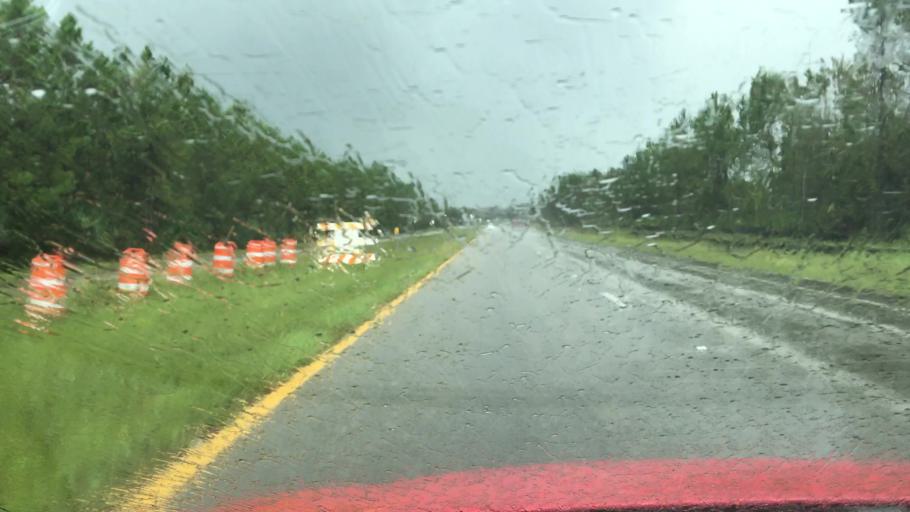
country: US
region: Florida
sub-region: Volusia County
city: Holly Hill
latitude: 29.2210
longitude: -81.0833
